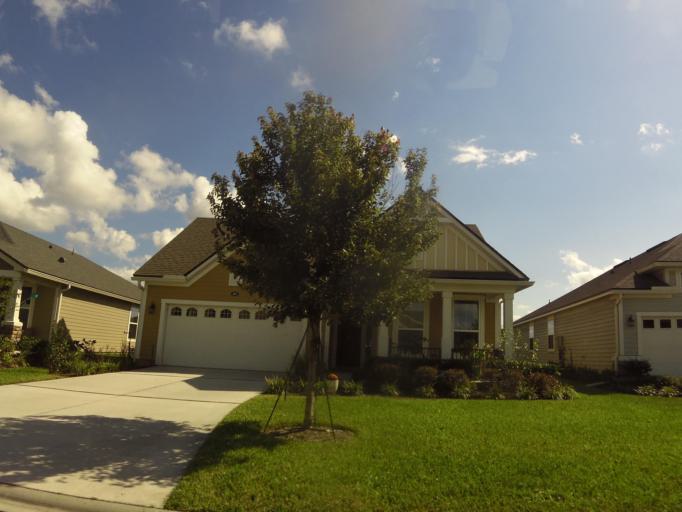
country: US
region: Florida
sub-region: Saint Johns County
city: Palm Valley
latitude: 30.0747
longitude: -81.4670
